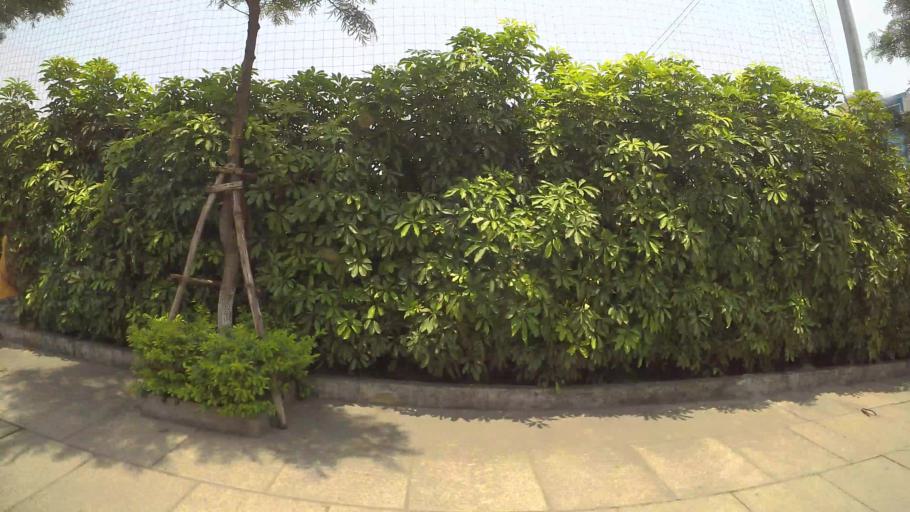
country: VN
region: Ha Noi
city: Trau Quy
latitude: 21.0332
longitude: 105.8981
